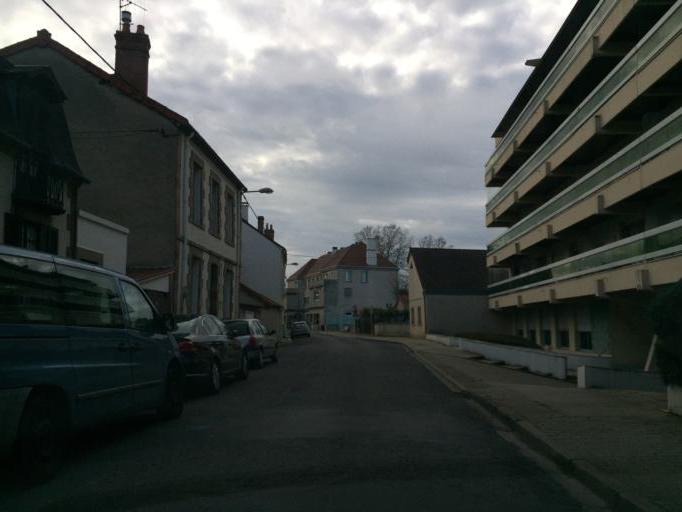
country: FR
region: Auvergne
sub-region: Departement de l'Allier
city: Moulins
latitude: 46.5716
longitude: 3.3371
